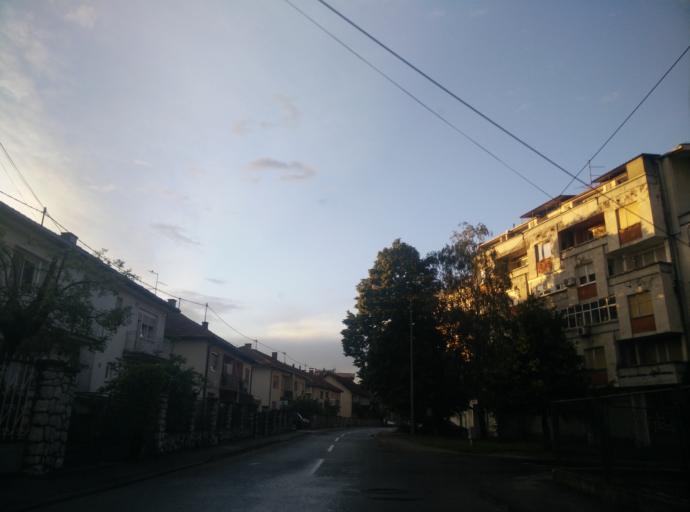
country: BA
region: Brcko
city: Brcko
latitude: 44.8683
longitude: 18.8144
